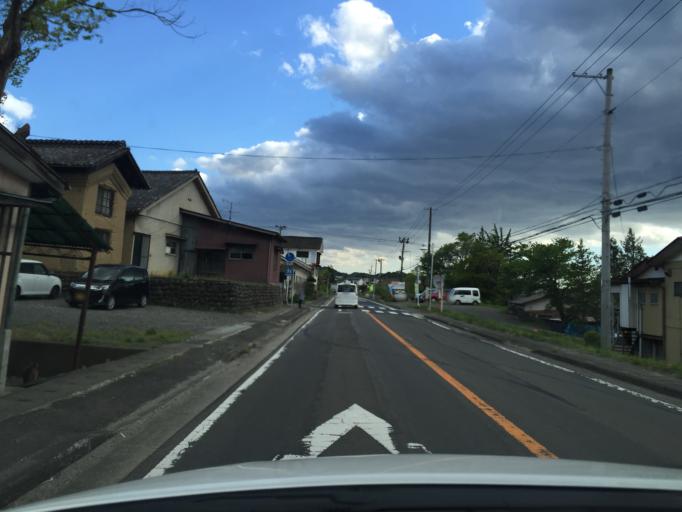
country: JP
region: Fukushima
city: Fukushima-shi
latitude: 37.6617
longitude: 140.5450
